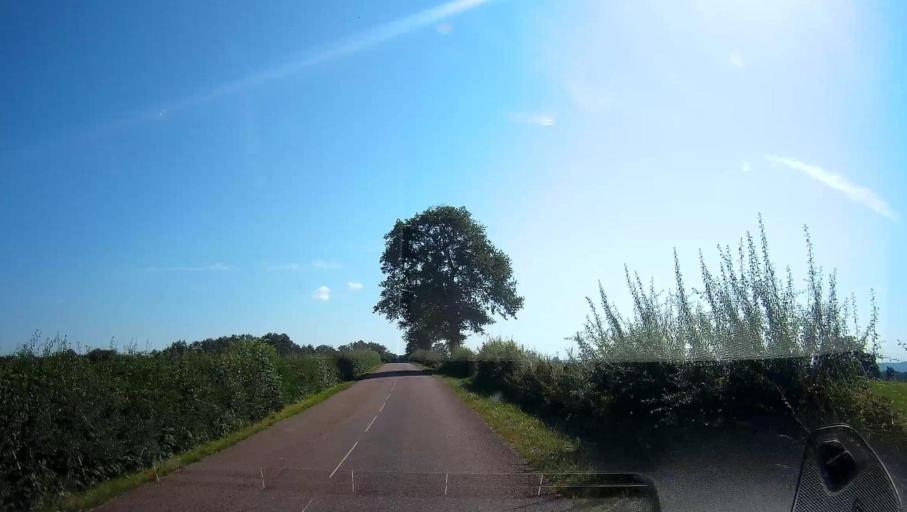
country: FR
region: Bourgogne
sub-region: Departement de Saone-et-Loire
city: Couches
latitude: 46.8836
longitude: 4.5380
